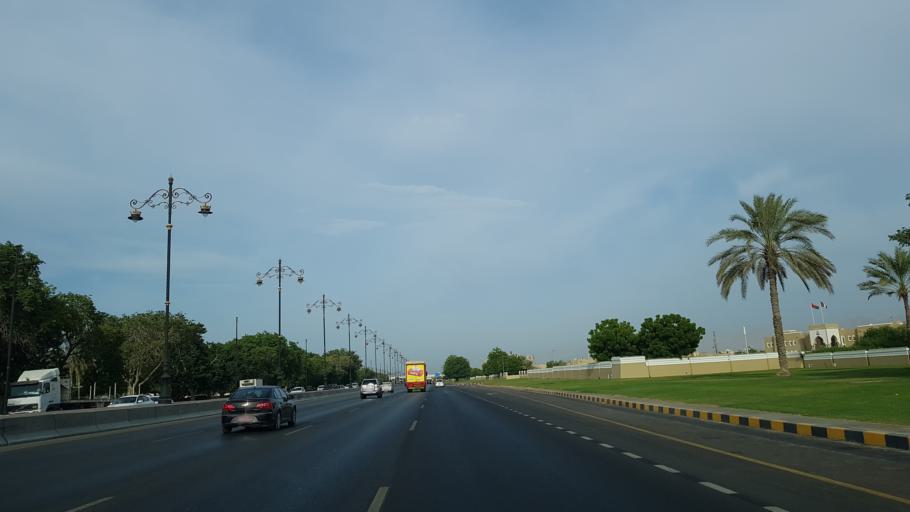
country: OM
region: Muhafazat Masqat
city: Bawshar
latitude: 23.5846
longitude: 58.2826
